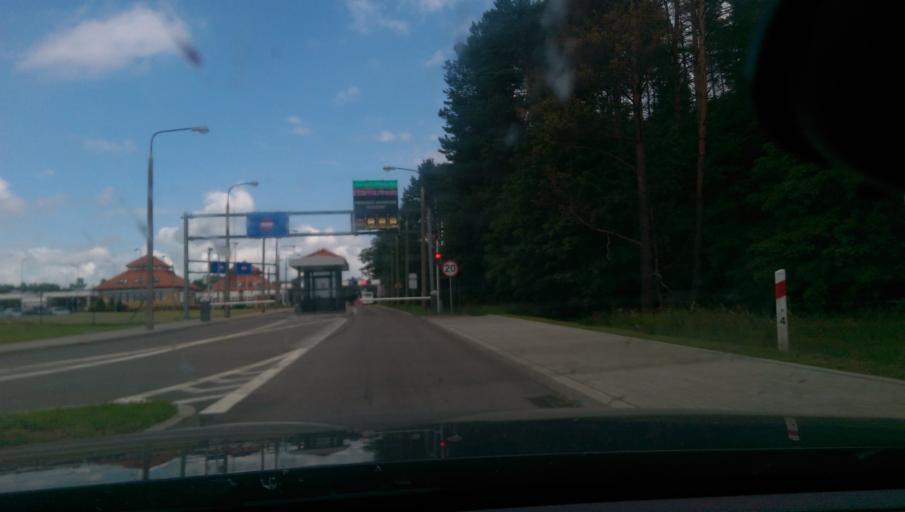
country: PL
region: Warmian-Masurian Voivodeship
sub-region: Powiat goldapski
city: Goldap
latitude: 54.3376
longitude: 22.2967
